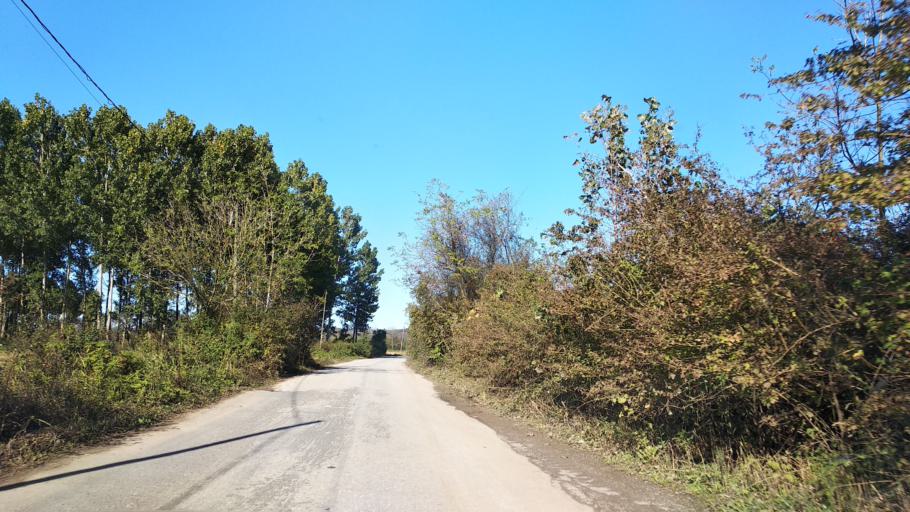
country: TR
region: Sakarya
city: Ortakoy
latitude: 41.0304
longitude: 30.6074
